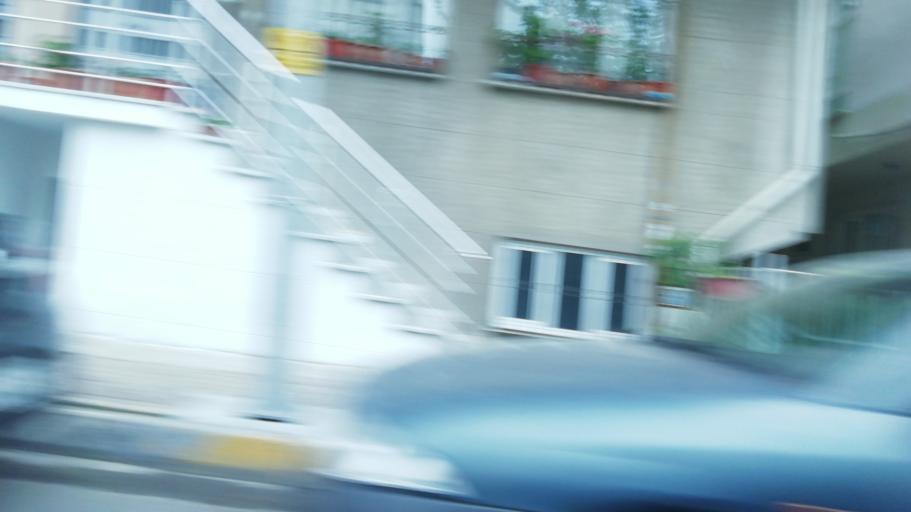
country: TR
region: Istanbul
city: Bagcilar
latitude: 41.0277
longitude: 28.8325
